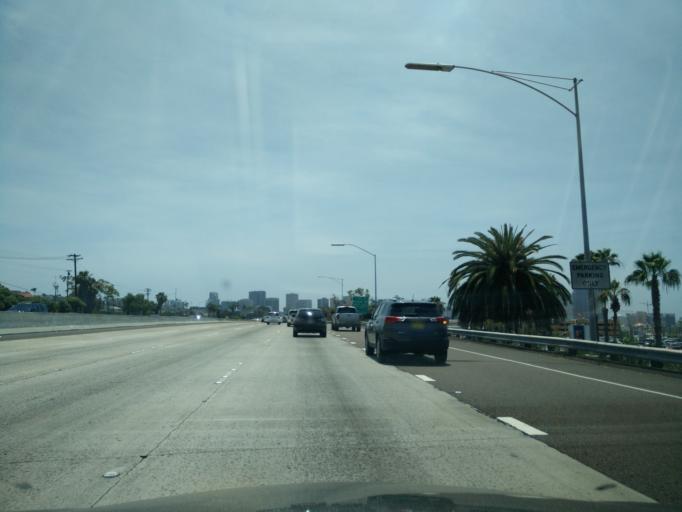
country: US
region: California
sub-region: San Diego County
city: San Diego
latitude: 32.7330
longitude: -117.1731
